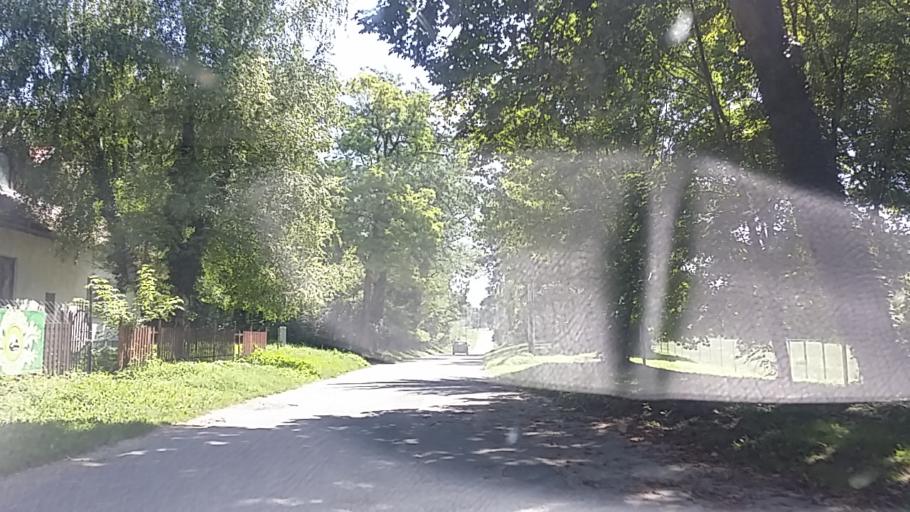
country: HU
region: Fejer
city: Deg
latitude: 46.8765
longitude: 18.4368
